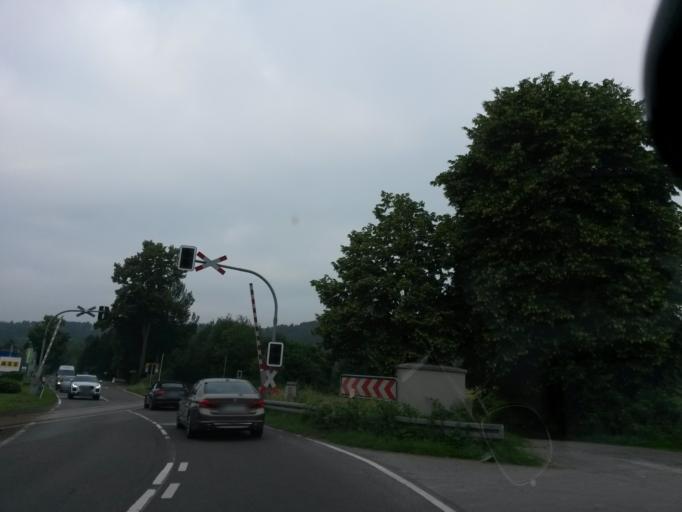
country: DE
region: North Rhine-Westphalia
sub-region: Regierungsbezirk Koln
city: Engelskirchen
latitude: 50.9766
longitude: 7.3522
